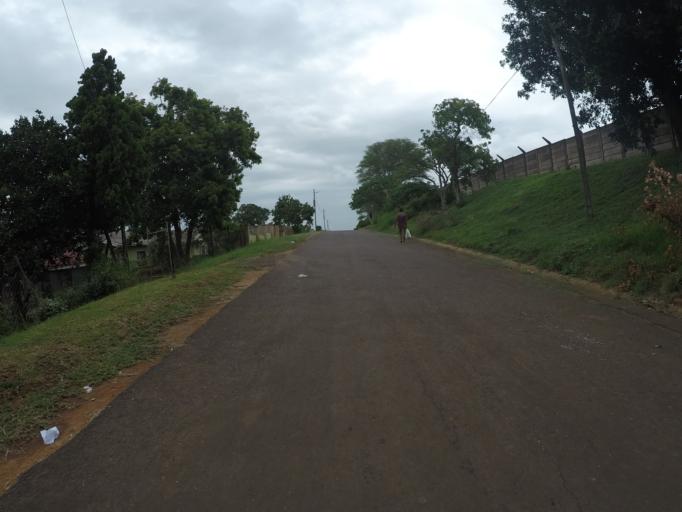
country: ZA
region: KwaZulu-Natal
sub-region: uThungulu District Municipality
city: Empangeni
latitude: -28.7758
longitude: 31.8629
